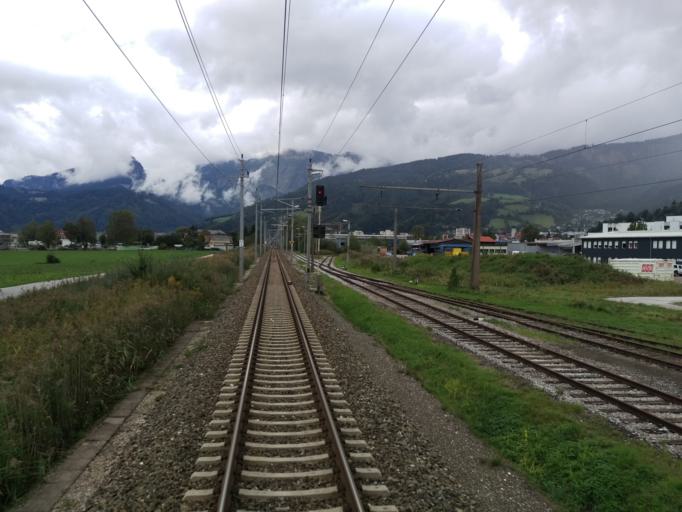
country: AT
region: Styria
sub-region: Politischer Bezirk Liezen
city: Liezen
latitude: 47.5576
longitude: 14.2520
